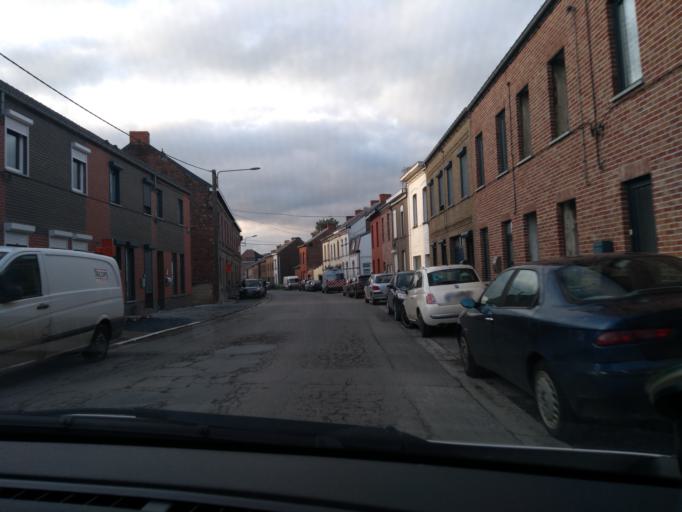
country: BE
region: Wallonia
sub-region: Province du Hainaut
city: Morlanwelz-Mariemont
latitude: 50.4290
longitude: 4.2141
